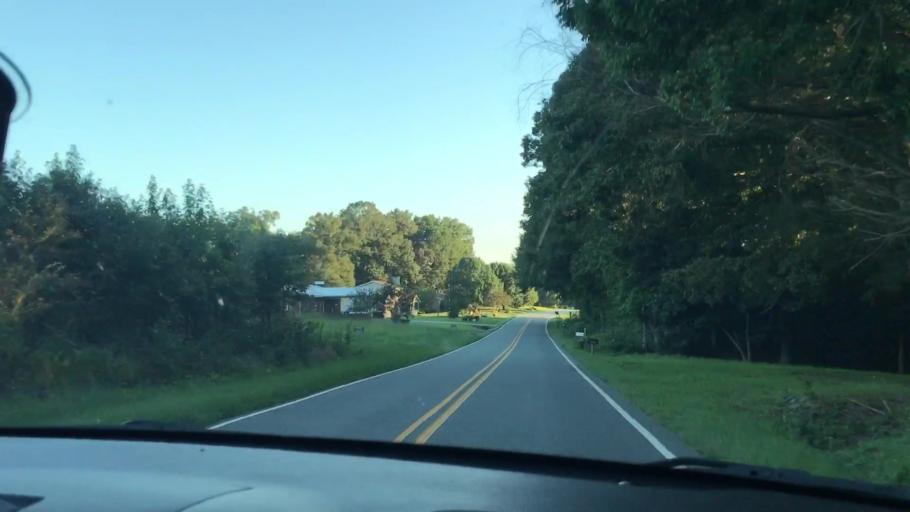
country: US
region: North Carolina
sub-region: Randolph County
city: Ramseur
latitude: 35.7950
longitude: -79.6435
